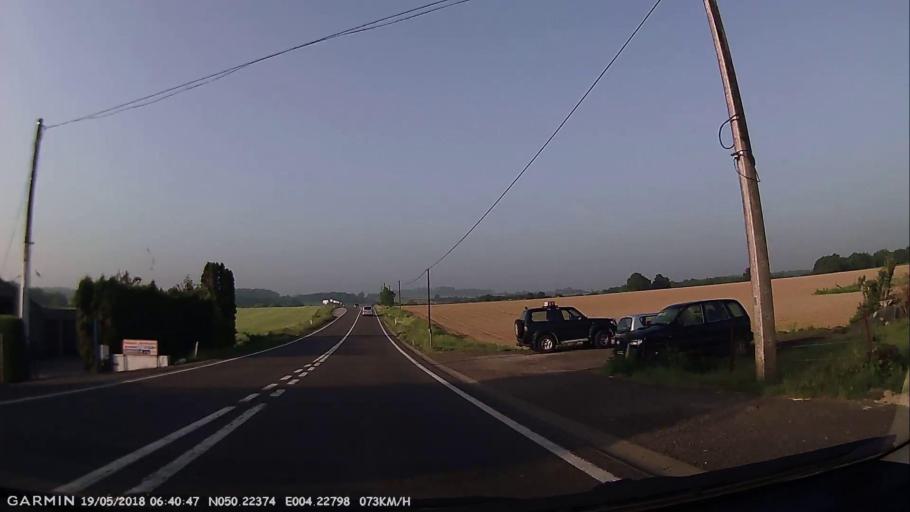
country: BE
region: Wallonia
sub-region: Province du Hainaut
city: Beaumont
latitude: 50.2235
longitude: 4.2279
